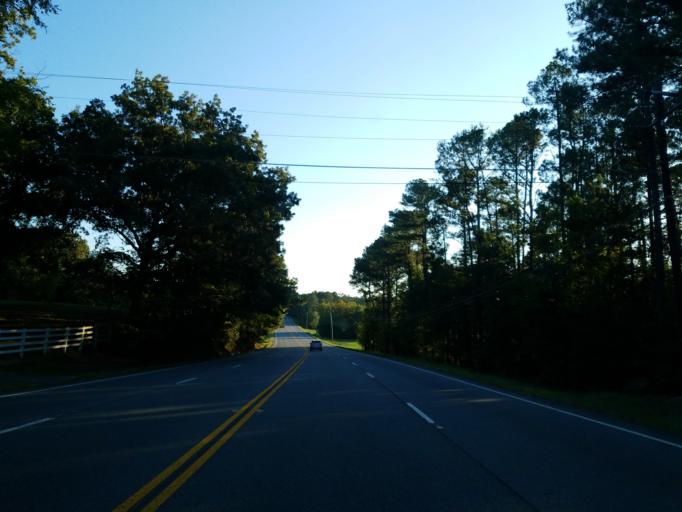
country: US
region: Georgia
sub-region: Bartow County
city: Cartersville
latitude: 34.2309
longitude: -84.7838
